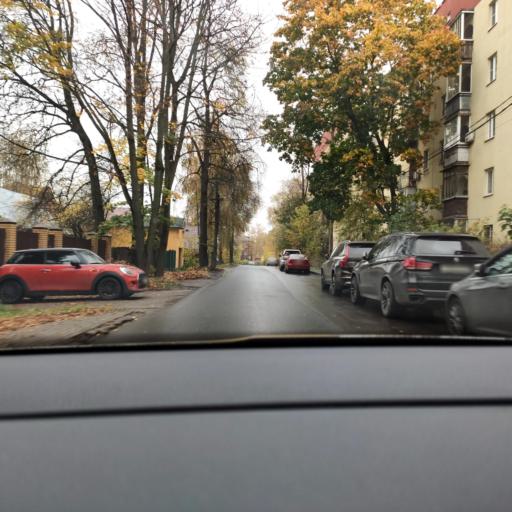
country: RU
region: Moskovskaya
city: Druzhba
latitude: 55.8864
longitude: 37.7536
